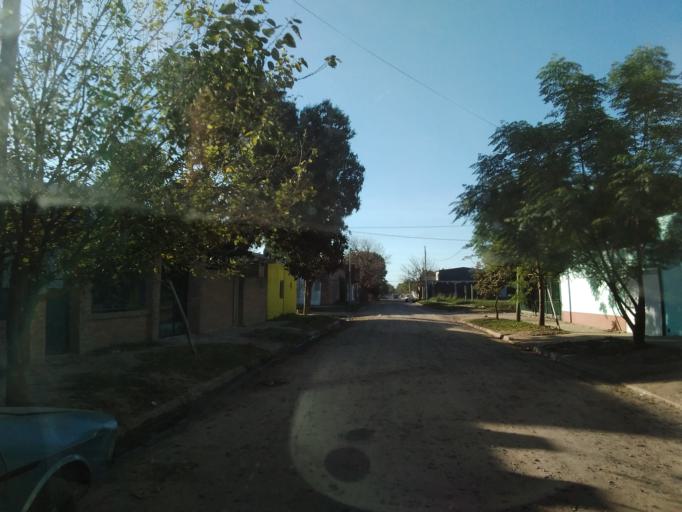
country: AR
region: Corrientes
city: Corrientes
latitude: -27.4998
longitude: -58.8356
